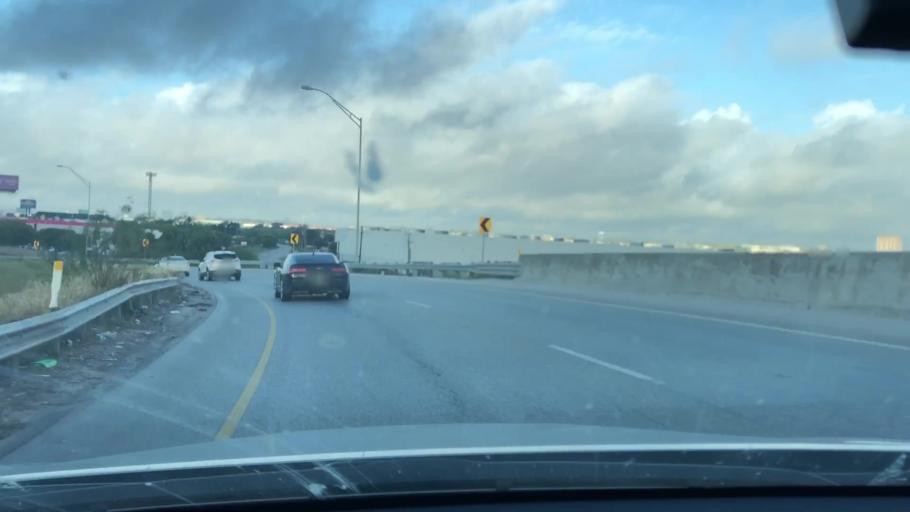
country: US
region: Texas
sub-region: Bexar County
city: Kirby
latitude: 29.4556
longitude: -98.4143
